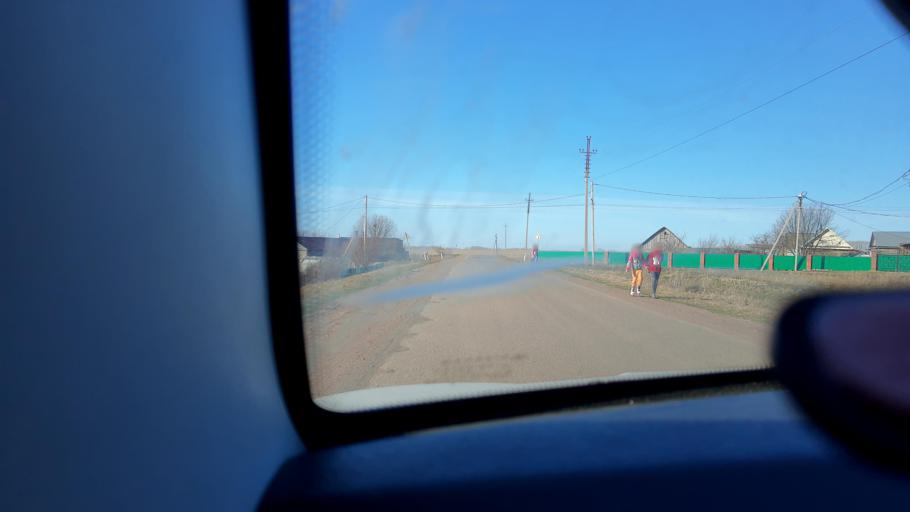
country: RU
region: Bashkortostan
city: Asanovo
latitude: 54.8430
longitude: 55.4588
